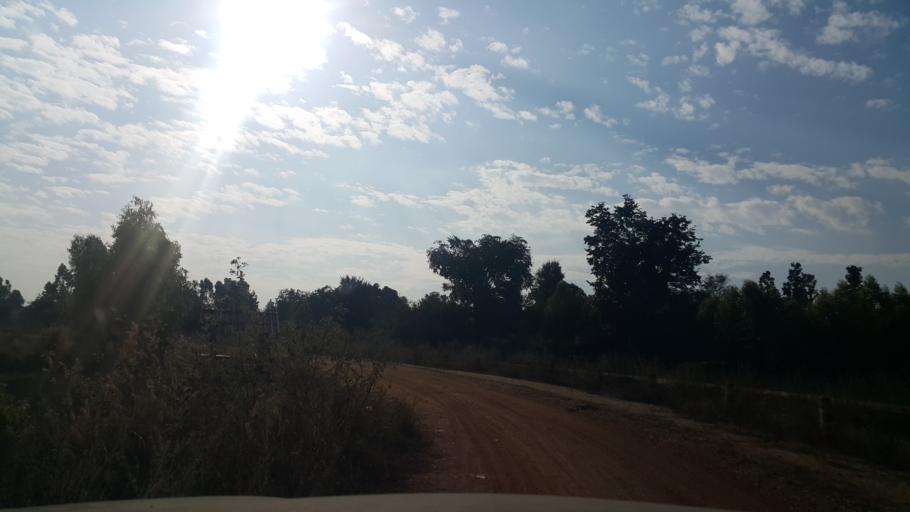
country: TH
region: Lampang
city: Ko Kha
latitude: 18.2414
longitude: 99.3594
